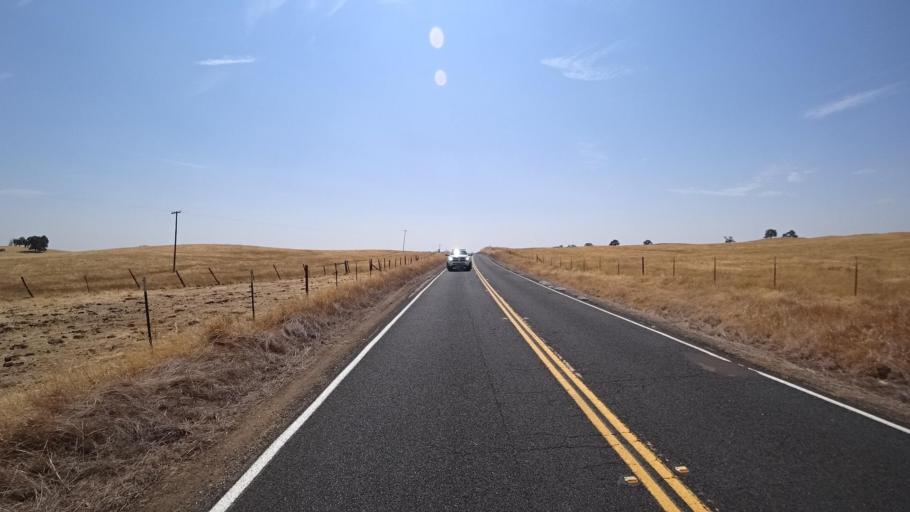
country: US
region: California
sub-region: Mariposa County
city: Mariposa
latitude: 37.4913
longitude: -120.1862
